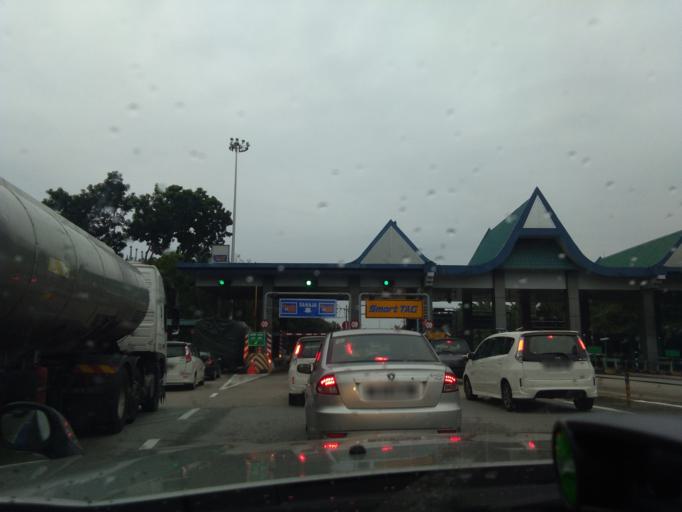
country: MY
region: Penang
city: Nibong Tebal
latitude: 5.1871
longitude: 100.4894
